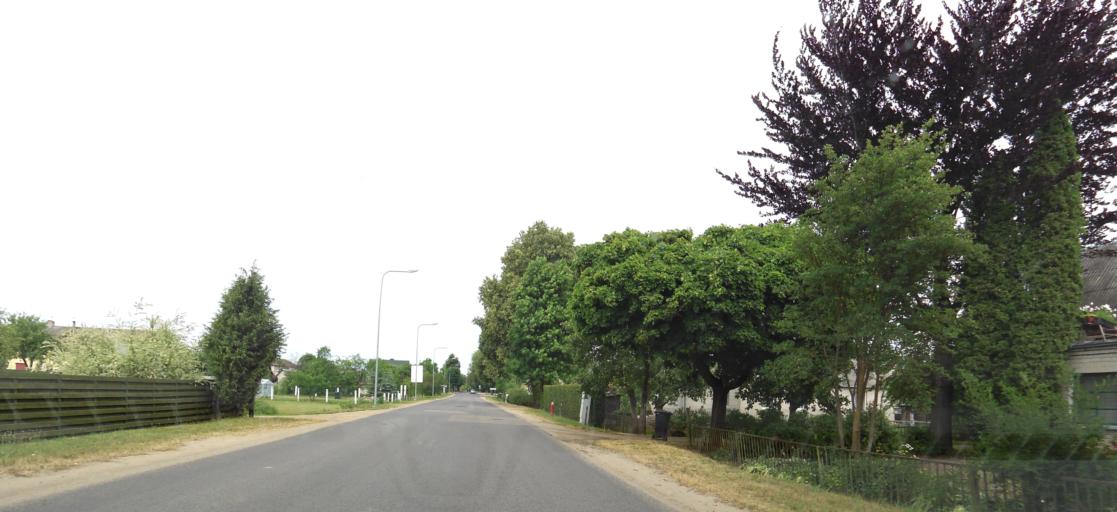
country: LT
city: Sirvintos
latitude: 55.0328
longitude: 24.9756
